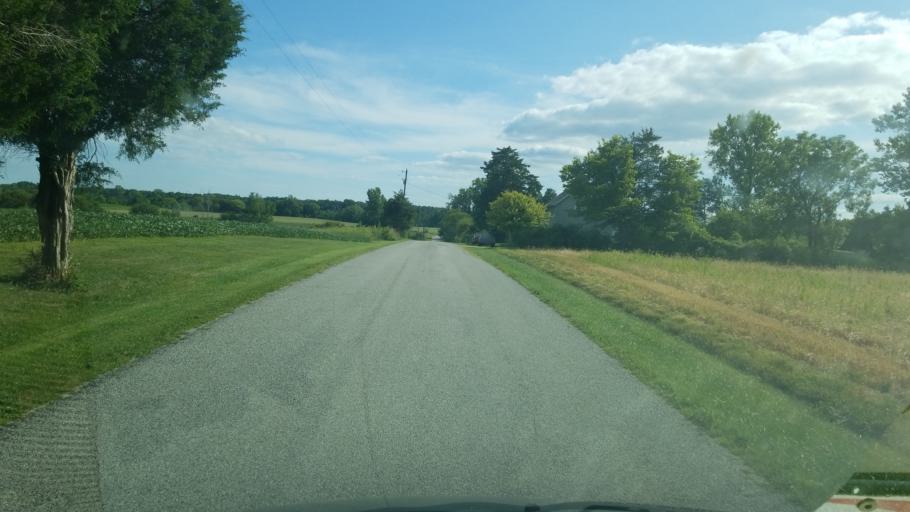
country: US
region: Ohio
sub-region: Champaign County
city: Saint Paris
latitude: 40.1523
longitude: -83.8650
